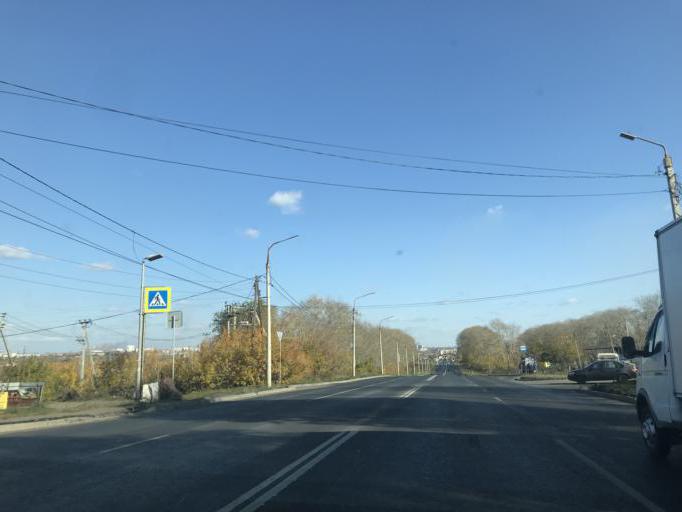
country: RU
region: Chelyabinsk
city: Roshchino
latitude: 55.2402
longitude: 61.3329
